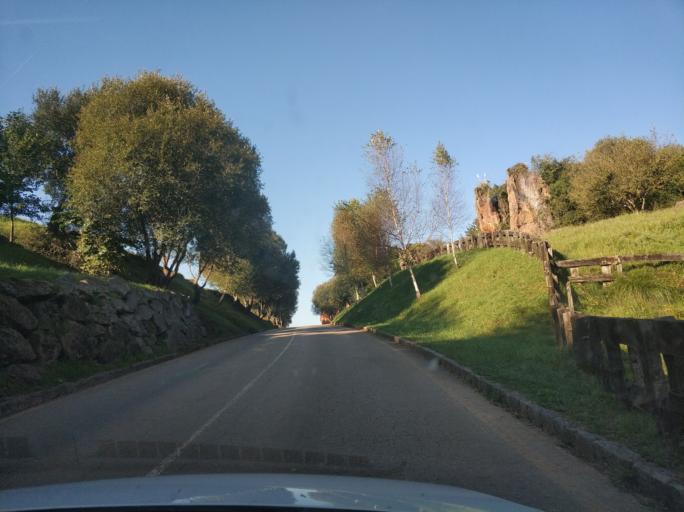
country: ES
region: Cantabria
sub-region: Provincia de Cantabria
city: Penagos
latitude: 43.3587
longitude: -3.8308
